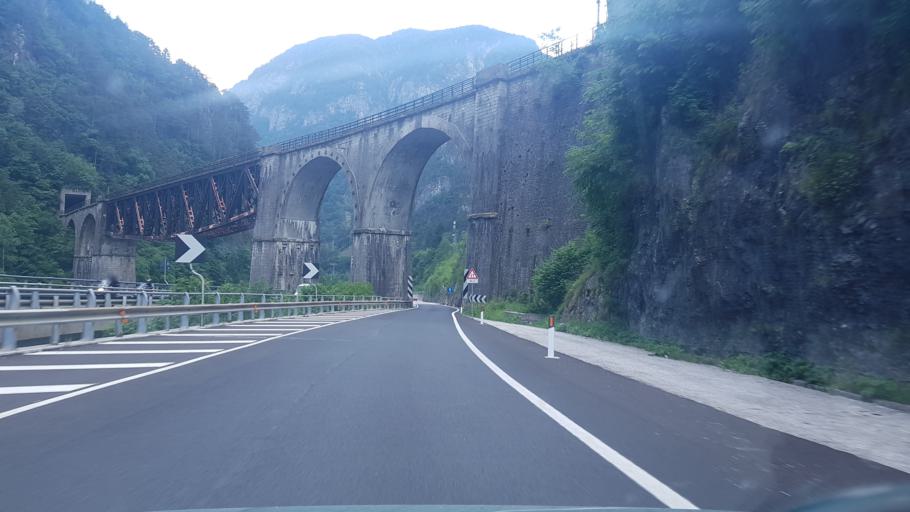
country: IT
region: Friuli Venezia Giulia
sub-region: Provincia di Udine
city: Dogna
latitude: 46.4669
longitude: 13.2939
